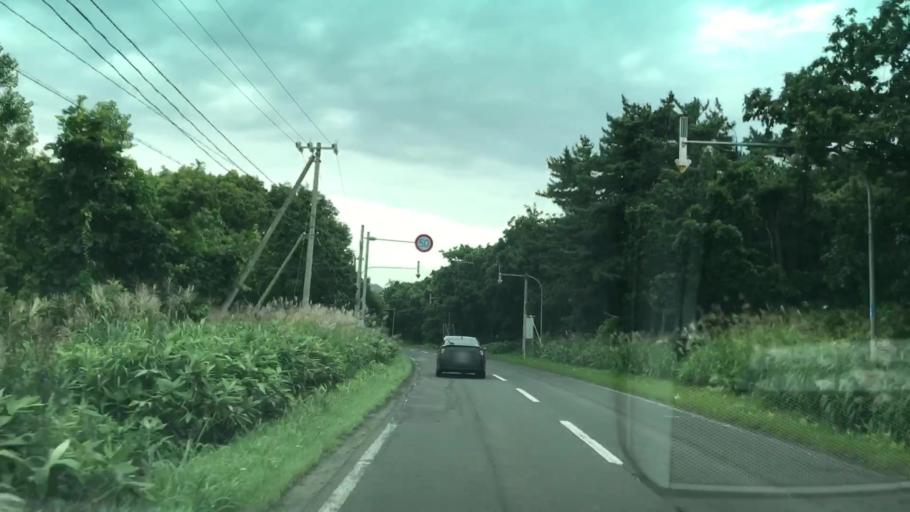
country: JP
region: Hokkaido
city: Iwanai
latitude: 42.8892
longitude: 140.3743
